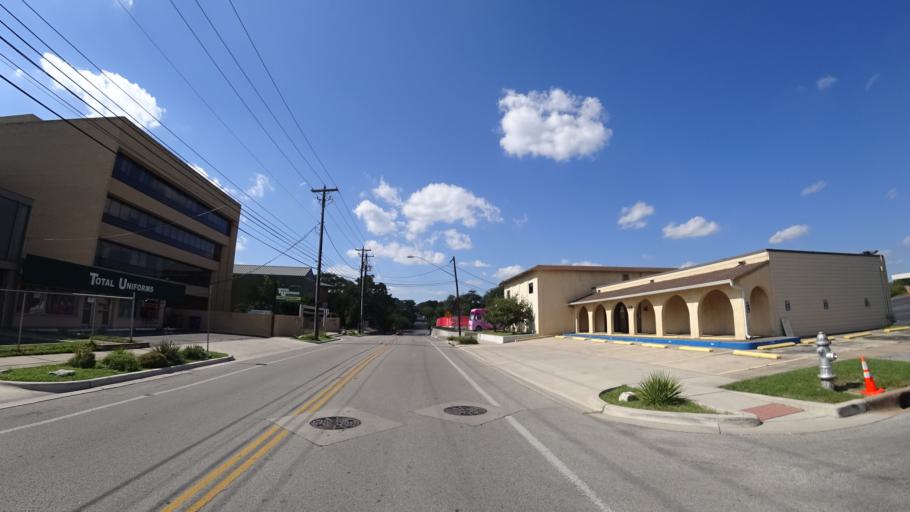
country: US
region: Texas
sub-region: Travis County
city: Austin
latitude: 30.3040
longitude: -97.7472
